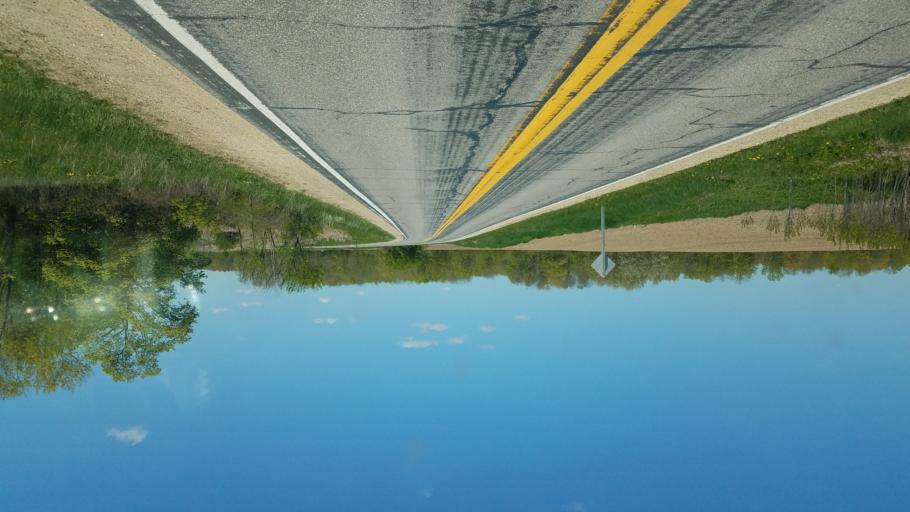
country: US
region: Wisconsin
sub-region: Vernon County
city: Hillsboro
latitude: 43.6089
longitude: -90.4648
